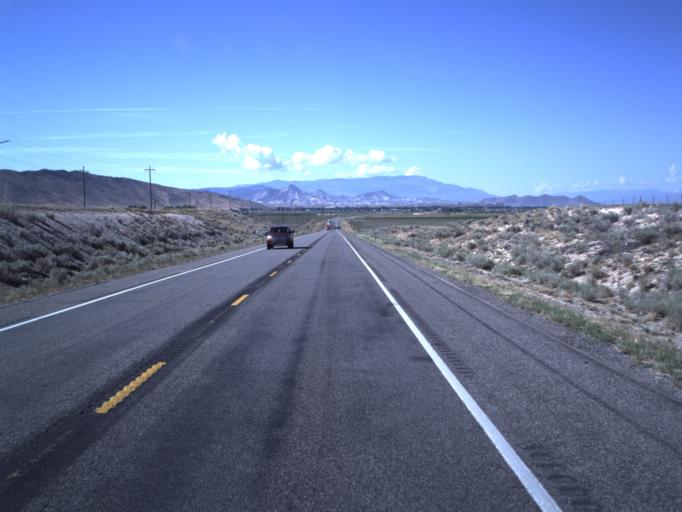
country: US
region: Utah
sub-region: Sevier County
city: Salina
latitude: 39.0176
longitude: -111.8341
